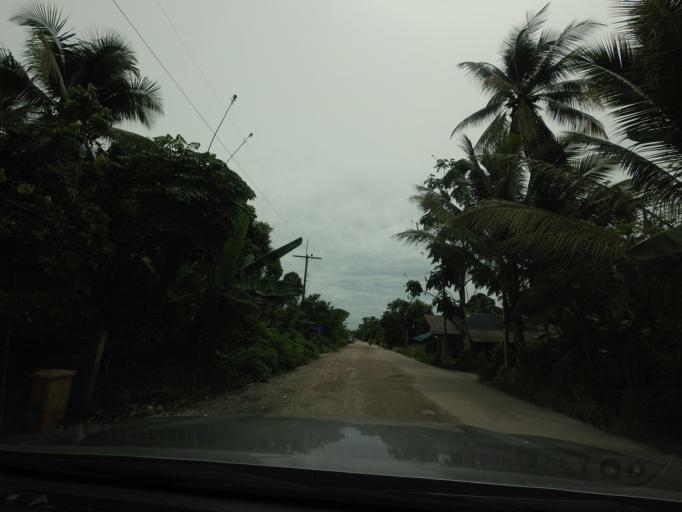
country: TH
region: Pattani
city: Sai Buri
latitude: 6.6565
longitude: 101.5528
